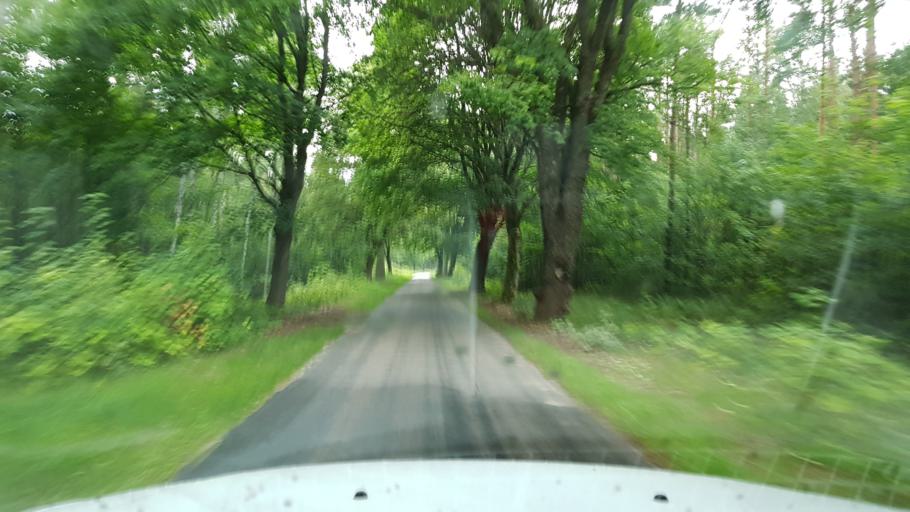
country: PL
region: West Pomeranian Voivodeship
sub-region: Powiat koszalinski
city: Bobolice
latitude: 53.8769
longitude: 16.6989
